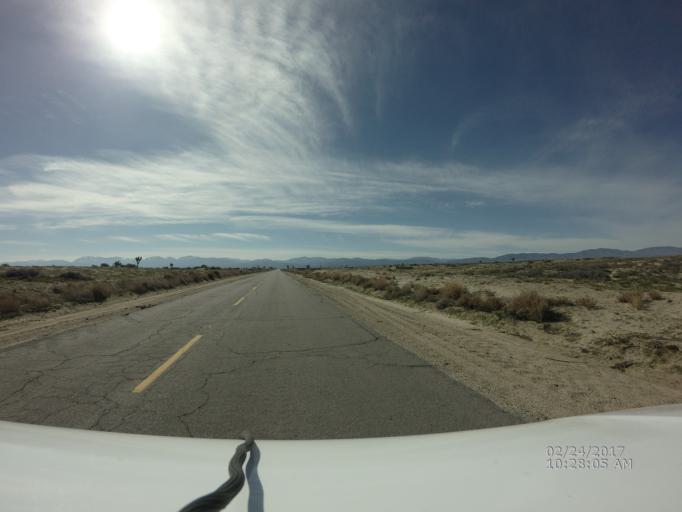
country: US
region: California
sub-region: Los Angeles County
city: Littlerock
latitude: 34.6485
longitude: -118.0052
